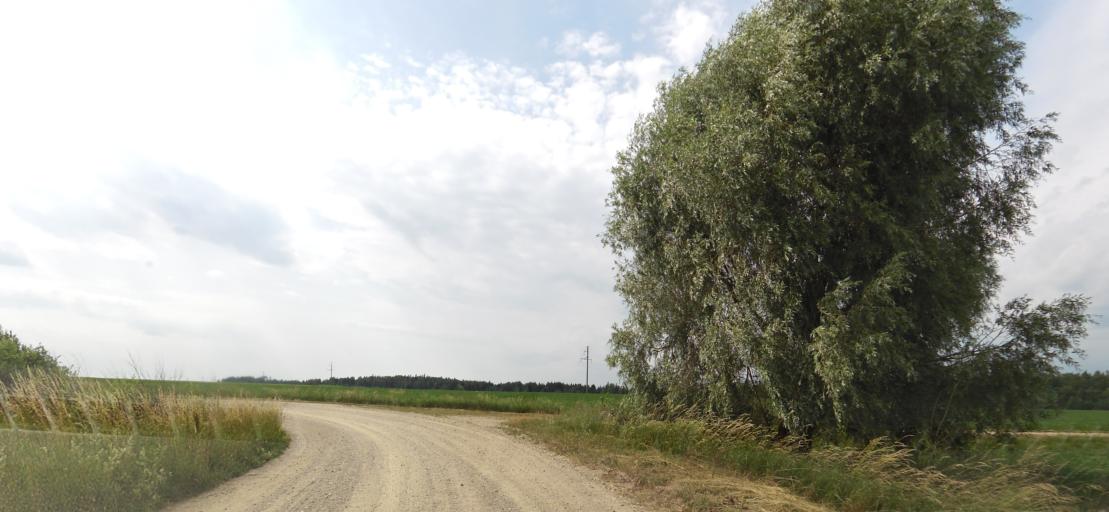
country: LT
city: Obeliai
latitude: 56.1872
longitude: 25.0240
